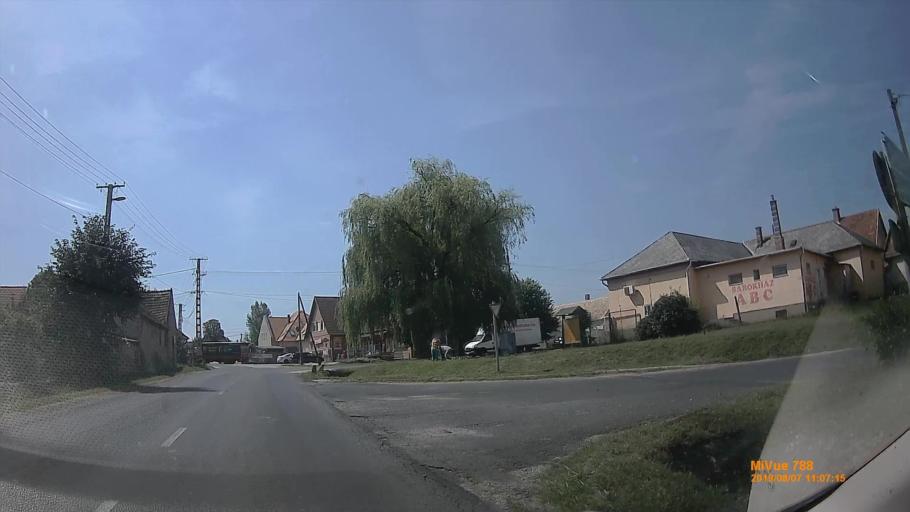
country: HU
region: Veszprem
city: Devecser
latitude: 47.0059
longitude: 17.4547
